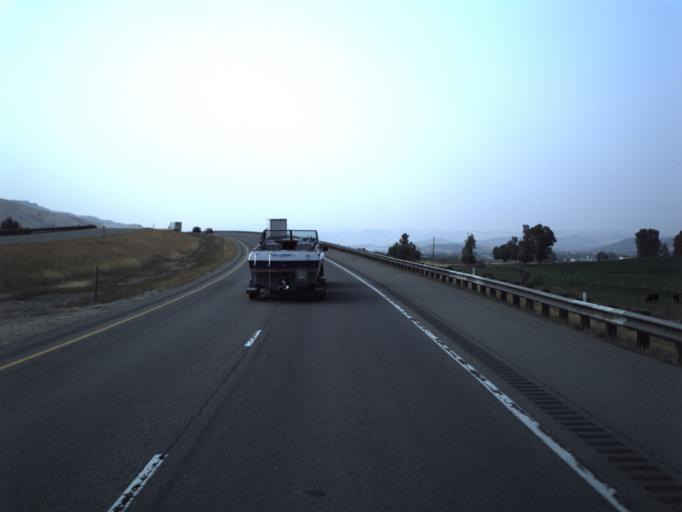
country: US
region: Utah
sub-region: Summit County
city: Coalville
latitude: 40.8436
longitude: -111.3871
